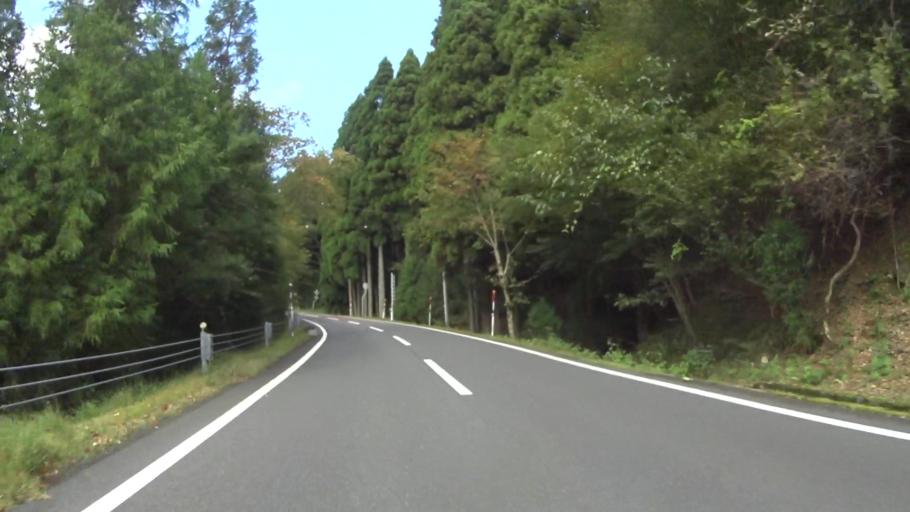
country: JP
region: Hyogo
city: Toyooka
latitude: 35.5193
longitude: 134.9894
